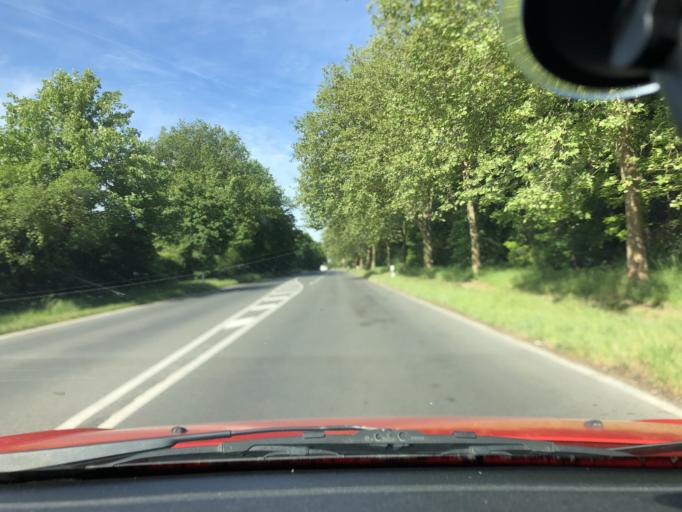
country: DE
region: North Rhine-Westphalia
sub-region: Regierungsbezirk Dusseldorf
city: Moers
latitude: 51.4933
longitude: 6.5997
